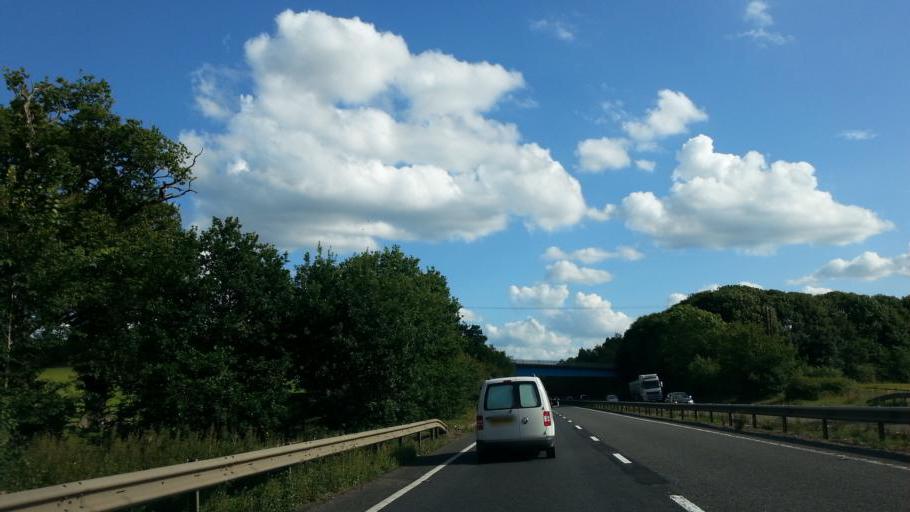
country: GB
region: England
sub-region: Suffolk
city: Needham Market
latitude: 52.1637
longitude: 1.0582
